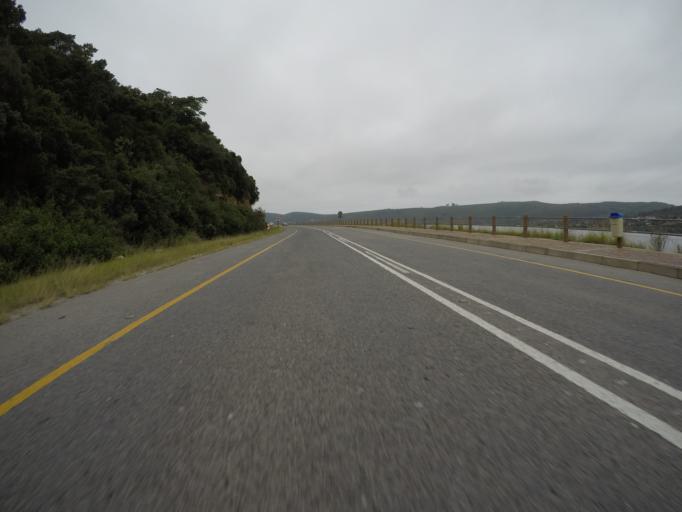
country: ZA
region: Western Cape
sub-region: Eden District Municipality
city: Knysna
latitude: -34.0306
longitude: 23.0062
